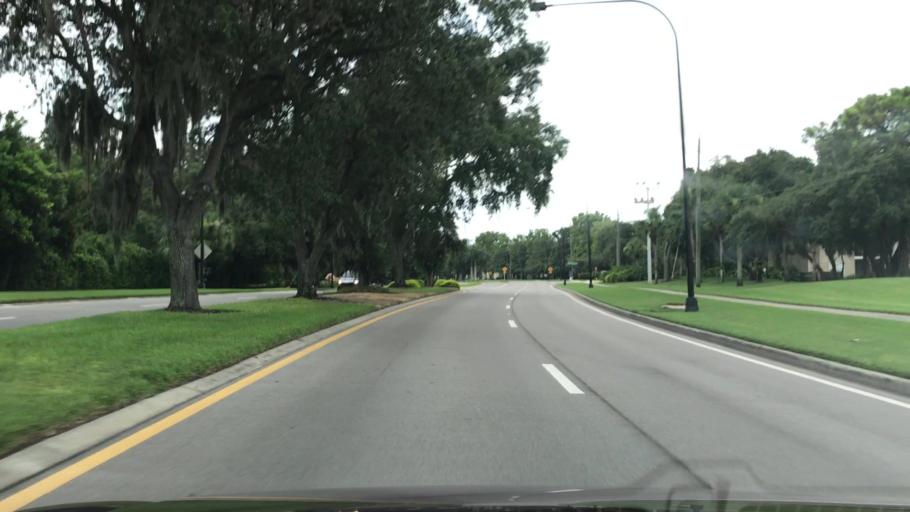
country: US
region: Florida
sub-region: Sarasota County
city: Vamo
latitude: 27.2362
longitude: -82.4875
